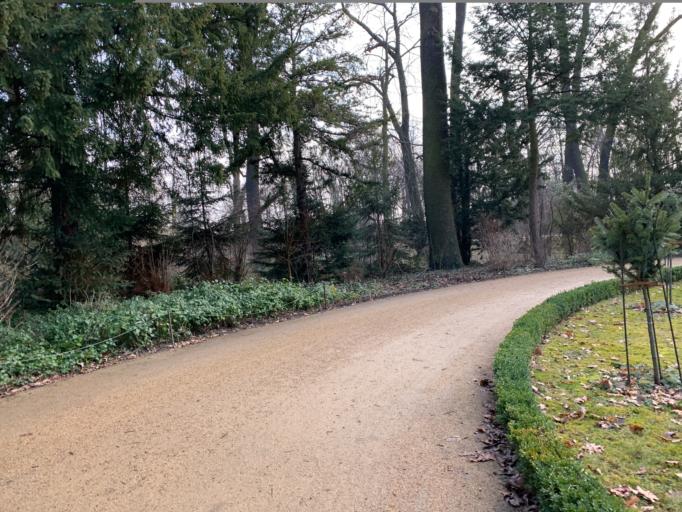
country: DE
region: Berlin
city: Charlottenburg-Nord
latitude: 52.5241
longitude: 13.2918
